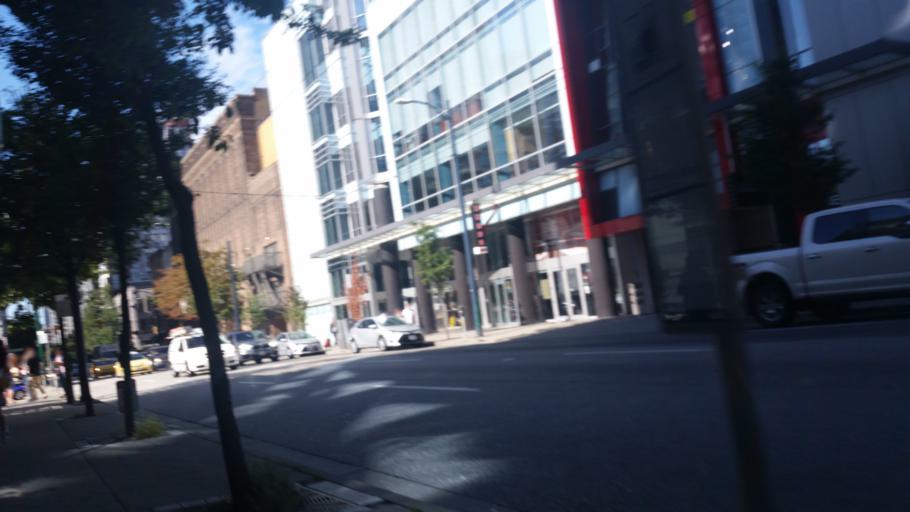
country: CA
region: British Columbia
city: West End
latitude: 49.2808
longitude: -123.1193
